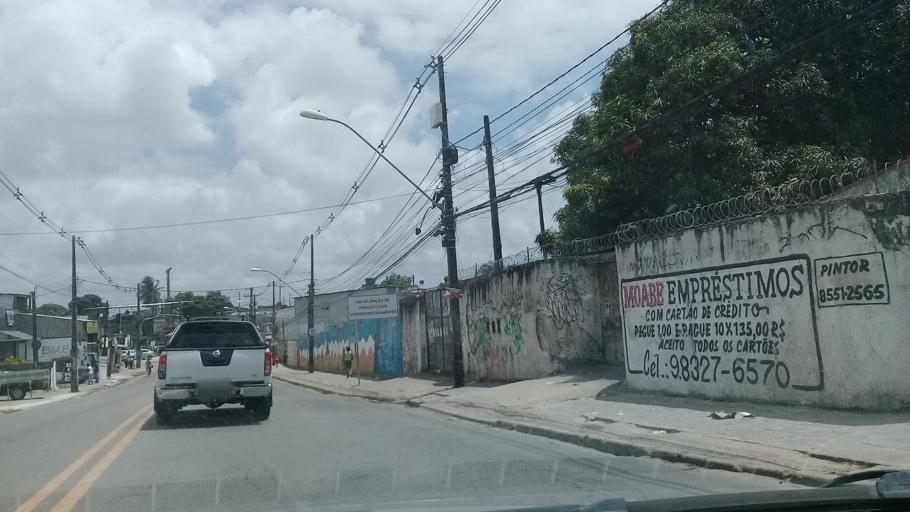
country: BR
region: Pernambuco
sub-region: Jaboatao Dos Guararapes
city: Jaboatao dos Guararapes
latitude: -8.1115
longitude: -34.9376
